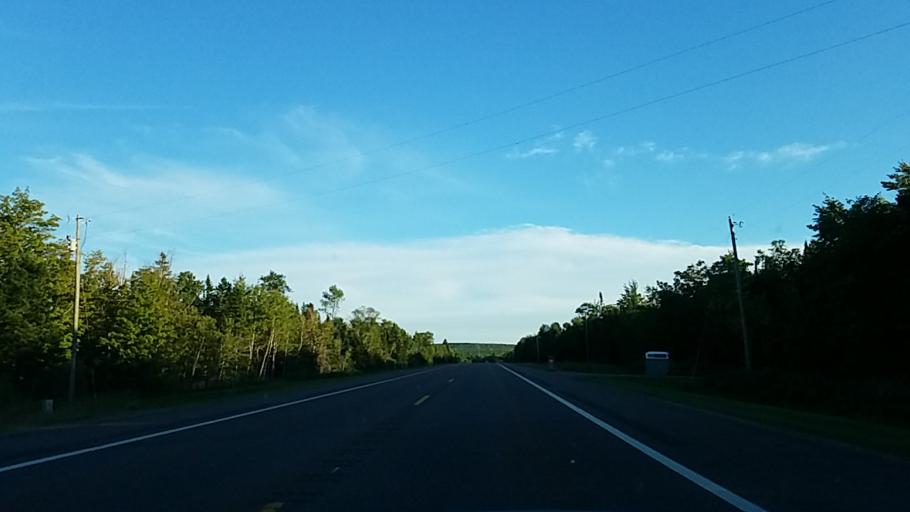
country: US
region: Michigan
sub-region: Alger County
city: Munising
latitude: 46.4530
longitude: -86.8892
